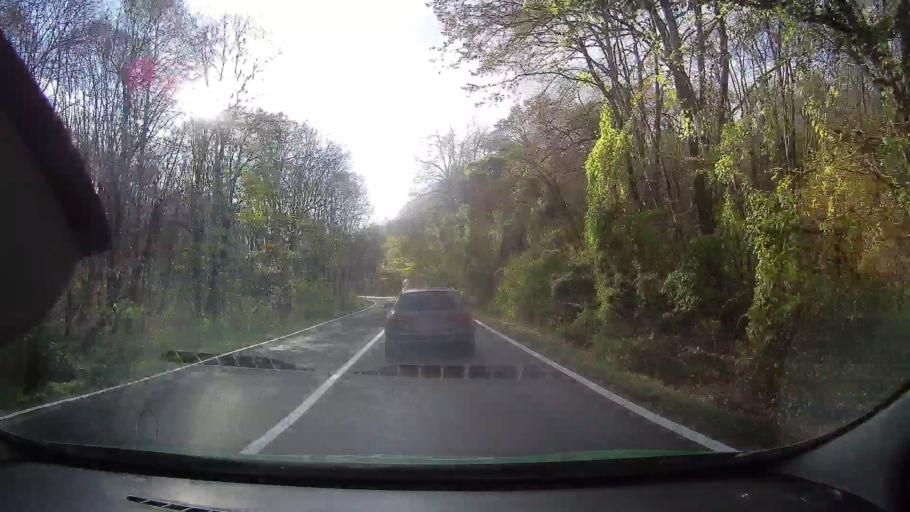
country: RO
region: Tulcea
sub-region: Comuna Ciucurova
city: Ciucurova
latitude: 44.9229
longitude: 28.4314
